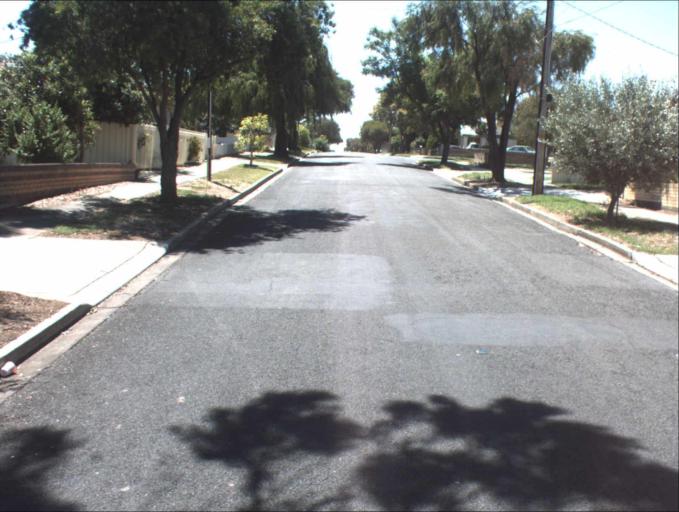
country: AU
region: South Australia
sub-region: Port Adelaide Enfield
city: Enfield
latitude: -34.8636
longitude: 138.6105
